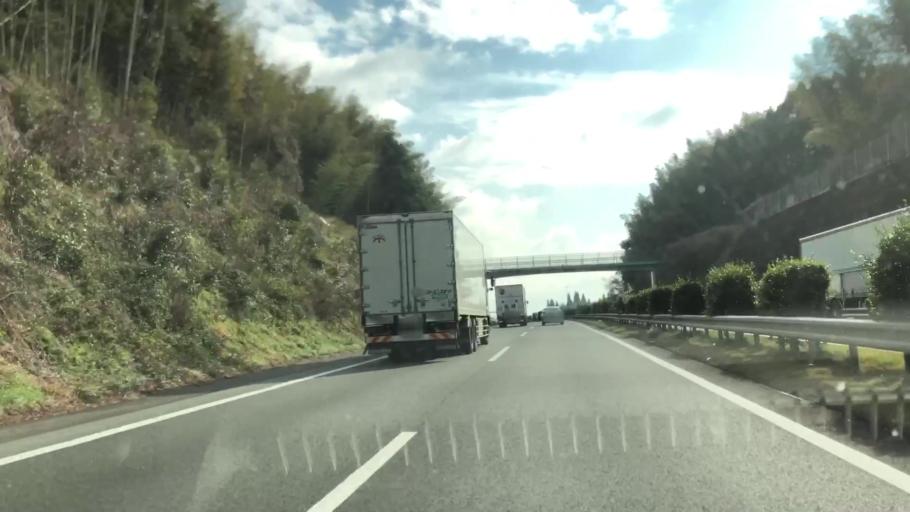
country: JP
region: Fukuoka
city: Setakamachi-takayanagi
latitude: 33.0909
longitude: 130.5389
